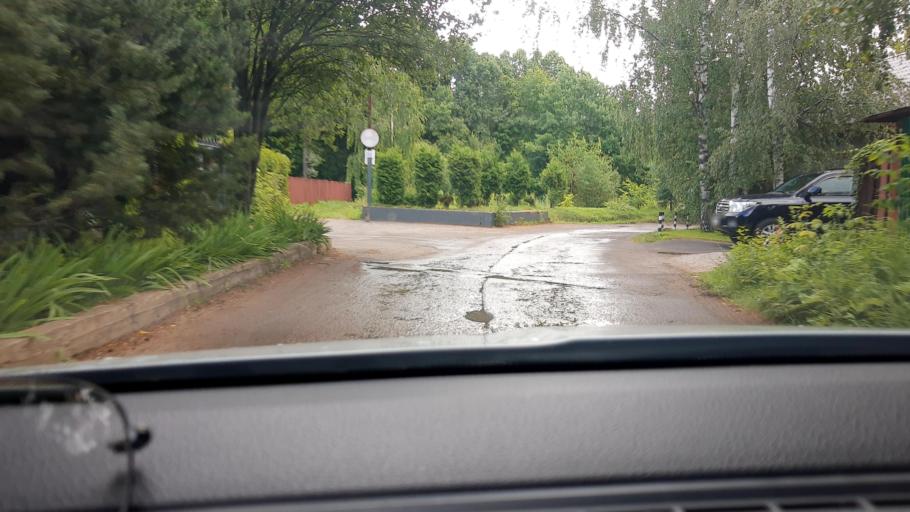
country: RU
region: Moskovskaya
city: Nemchinovka
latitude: 55.7355
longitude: 37.3531
